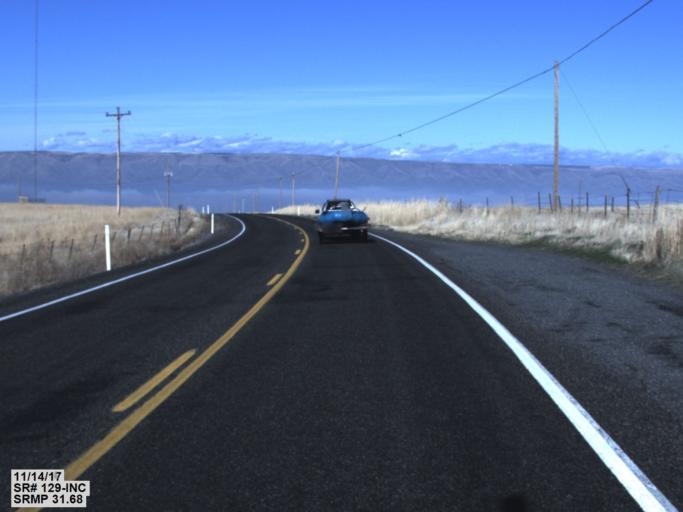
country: US
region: Washington
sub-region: Asotin County
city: Asotin
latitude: 46.3146
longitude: -117.0395
